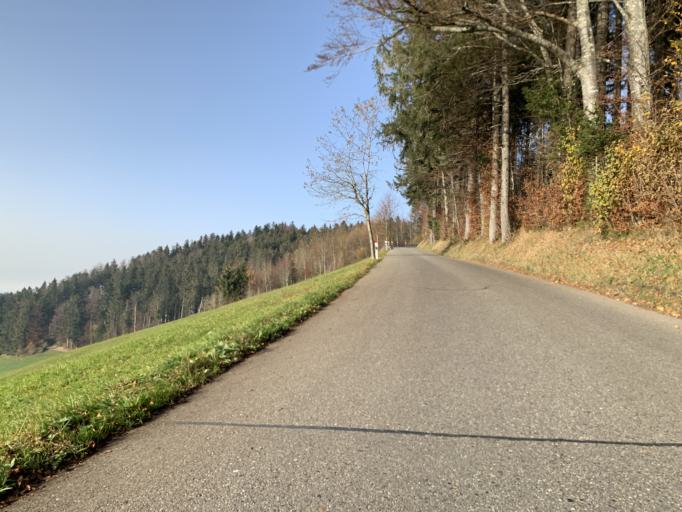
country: CH
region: Zurich
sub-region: Bezirk Hinwil
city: Hadlikon
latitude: 47.3038
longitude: 8.8857
